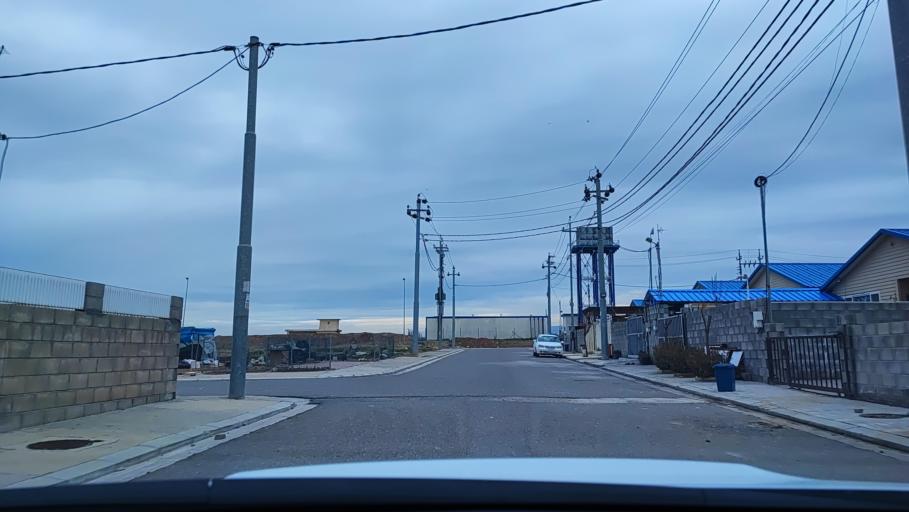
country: IQ
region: Arbil
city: Erbil
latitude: 36.2856
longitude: 44.0837
